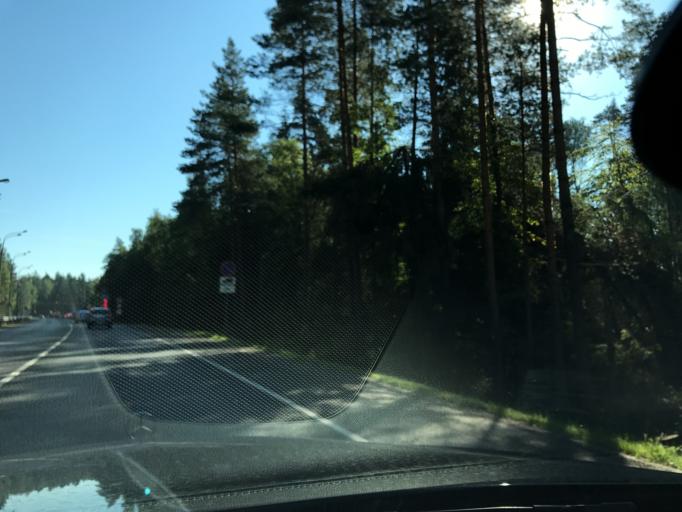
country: RU
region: Moskovskaya
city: Chernogolovka
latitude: 55.9833
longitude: 38.3338
